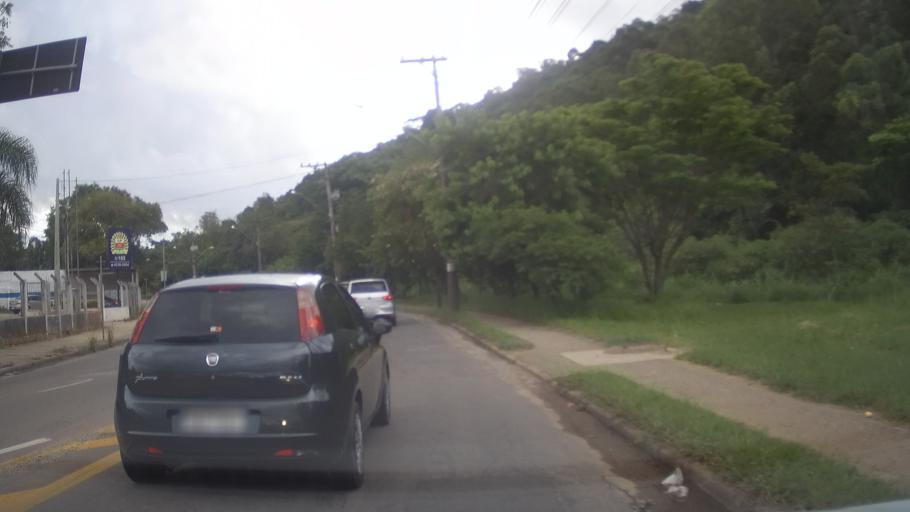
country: BR
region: Sao Paulo
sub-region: Campo Limpo Paulista
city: Campo Limpo Paulista
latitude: -23.2088
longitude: -46.7709
